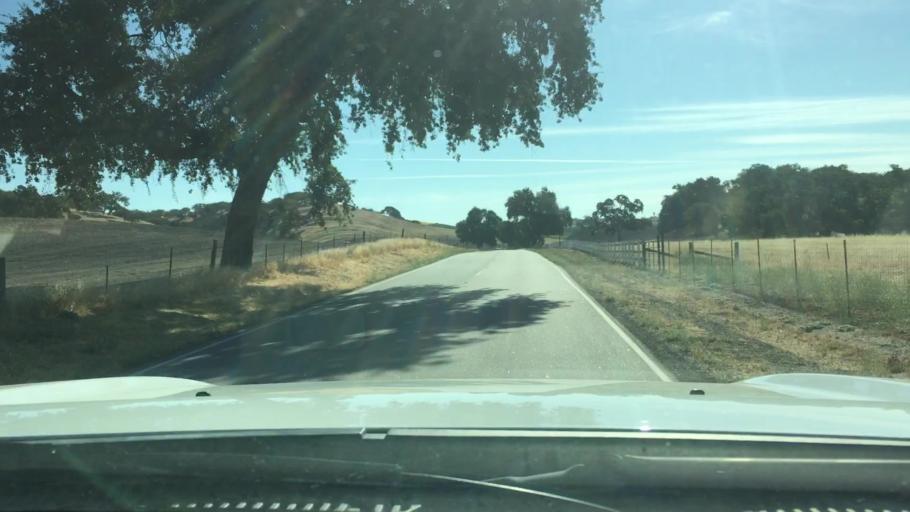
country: US
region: California
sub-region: San Luis Obispo County
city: Templeton
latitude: 35.5636
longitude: -120.6601
